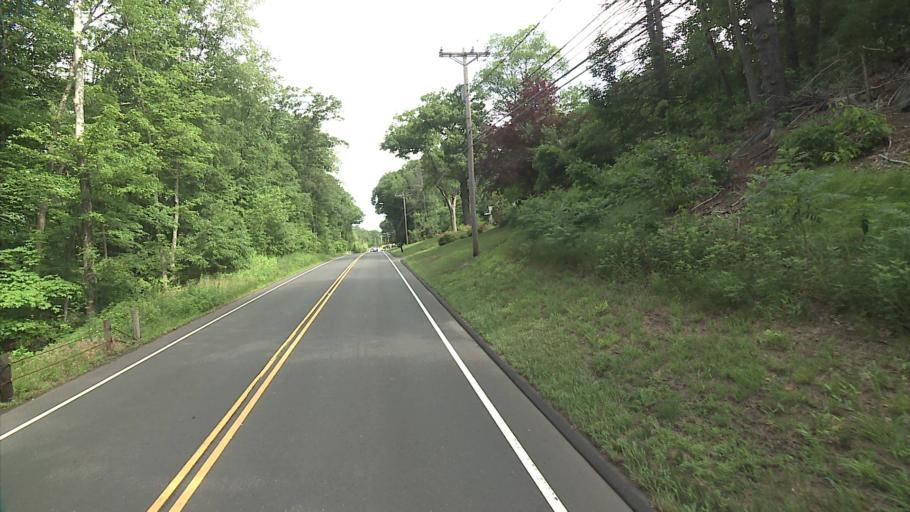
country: US
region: Connecticut
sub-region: Litchfield County
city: Oakville
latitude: 41.5614
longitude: -73.0948
